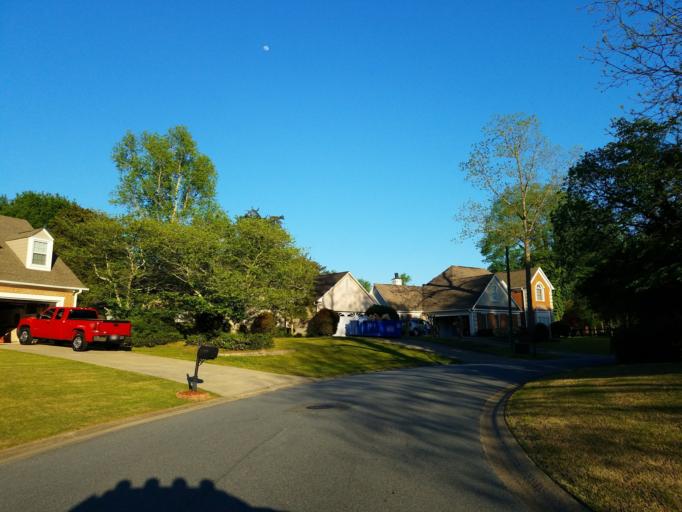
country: US
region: Georgia
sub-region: Cobb County
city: Powder Springs
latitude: 33.9231
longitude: -84.6371
